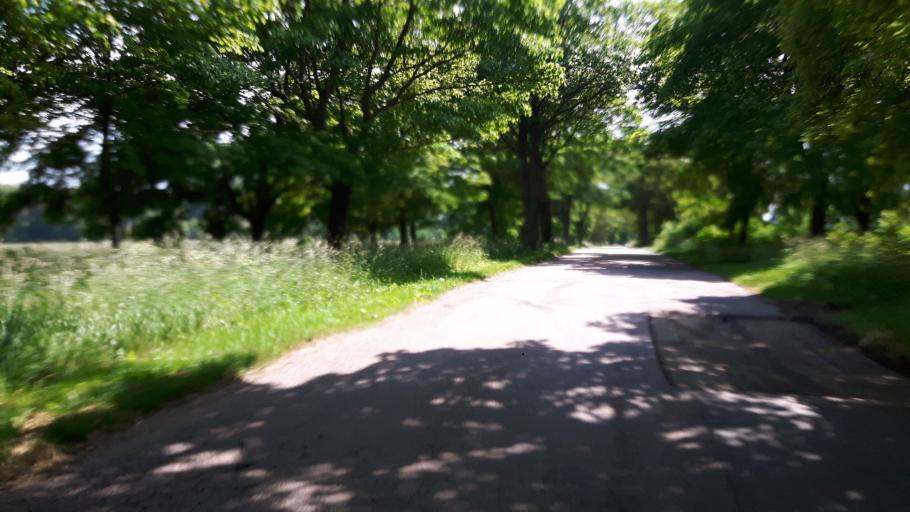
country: PL
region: Pomeranian Voivodeship
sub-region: Powiat wejherowski
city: Choczewo
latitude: 54.7428
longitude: 17.8120
